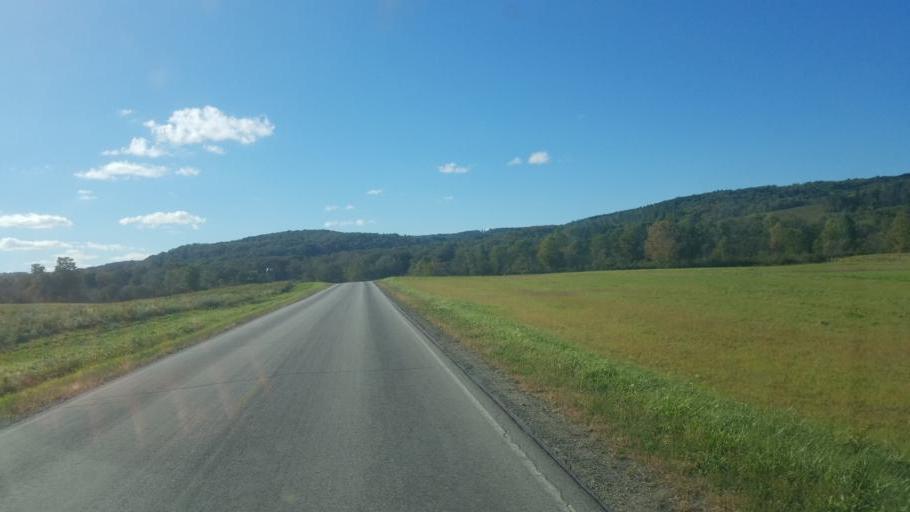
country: US
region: New York
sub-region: Allegany County
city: Cuba
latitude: 42.2756
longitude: -78.2129
